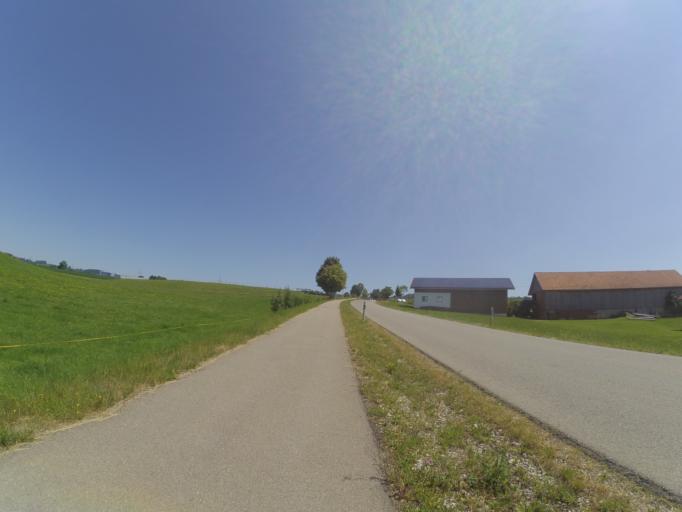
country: DE
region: Bavaria
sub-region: Swabia
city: Haldenwang
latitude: 47.7945
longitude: 10.3291
